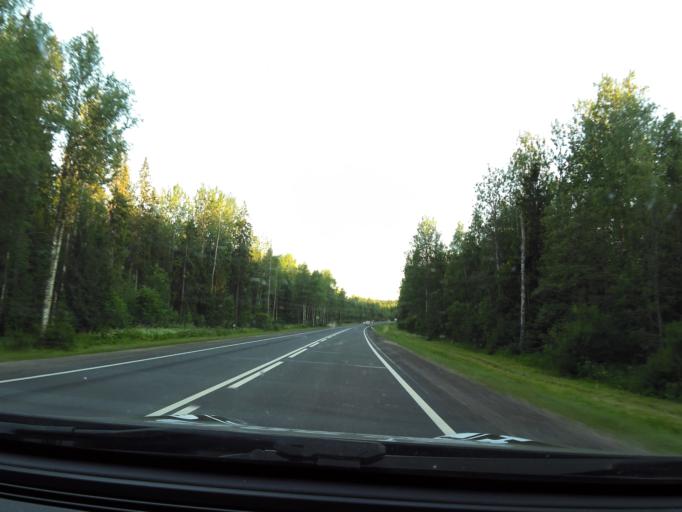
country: RU
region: Jaroslavl
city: Prechistoye
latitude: 58.5085
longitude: 40.3449
